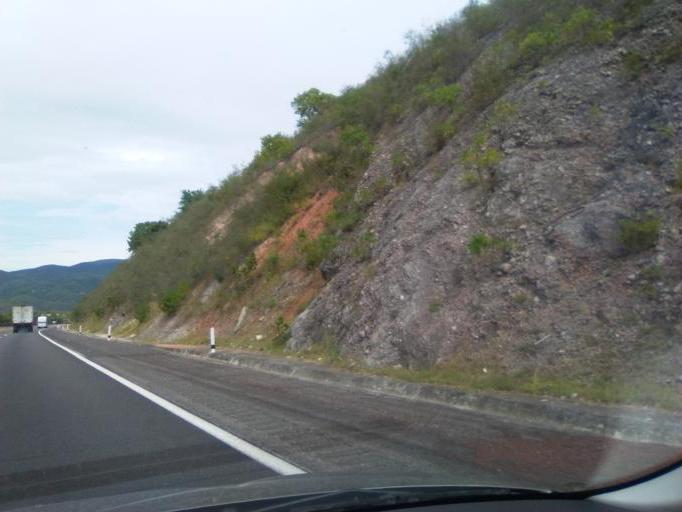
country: MX
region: Guerrero
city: Zumpango del Rio
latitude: 17.6224
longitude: -99.5166
